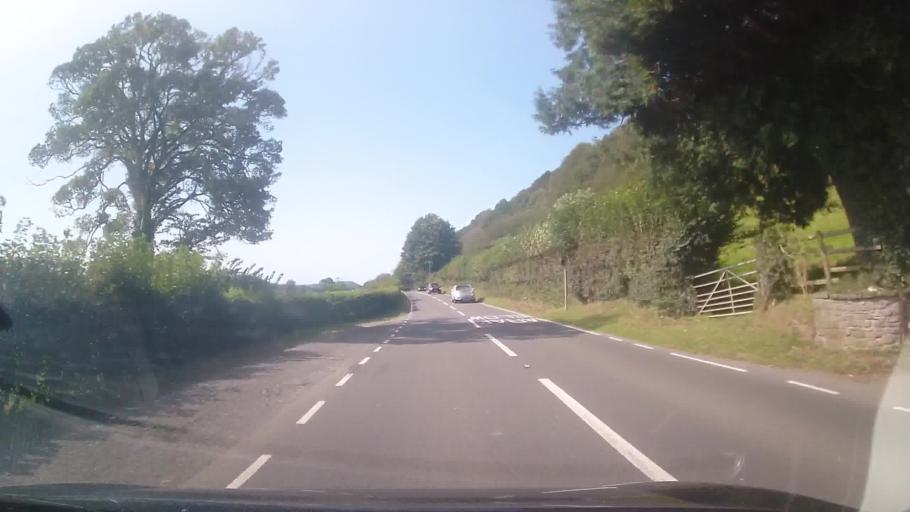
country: GB
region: Wales
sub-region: Carmarthenshire
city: Llanddarog
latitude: 51.8715
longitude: -4.2211
